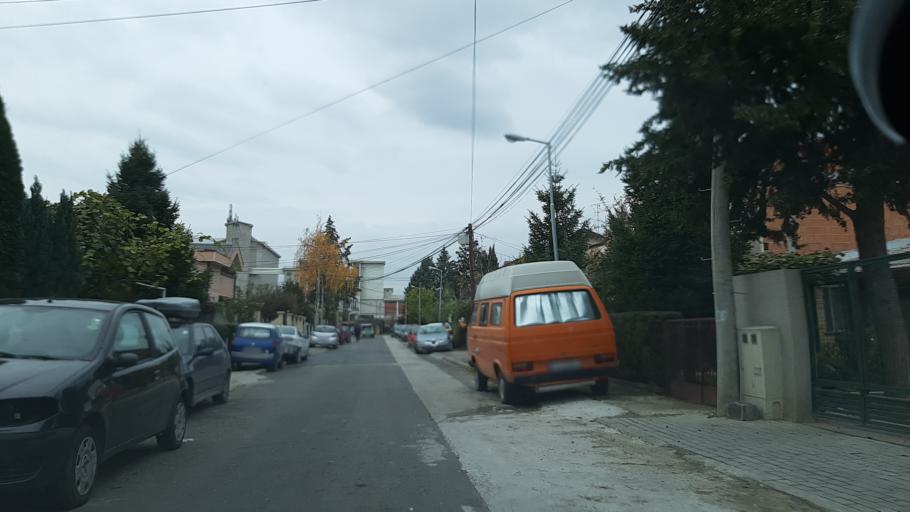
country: MK
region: Kisela Voda
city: Usje
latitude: 41.9750
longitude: 21.4657
